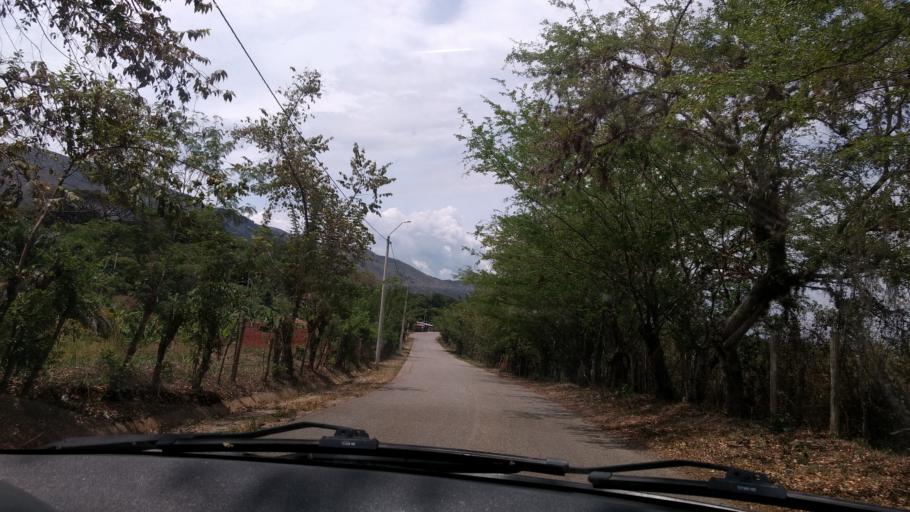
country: CO
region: Cauca
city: Buenos Aires
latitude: 3.0510
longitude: -76.6566
